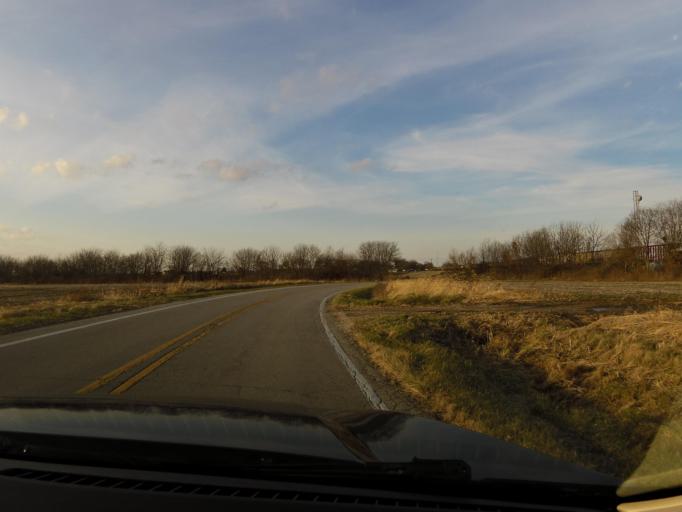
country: US
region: Illinois
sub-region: Fayette County
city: Vandalia
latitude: 38.9476
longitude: -89.1567
